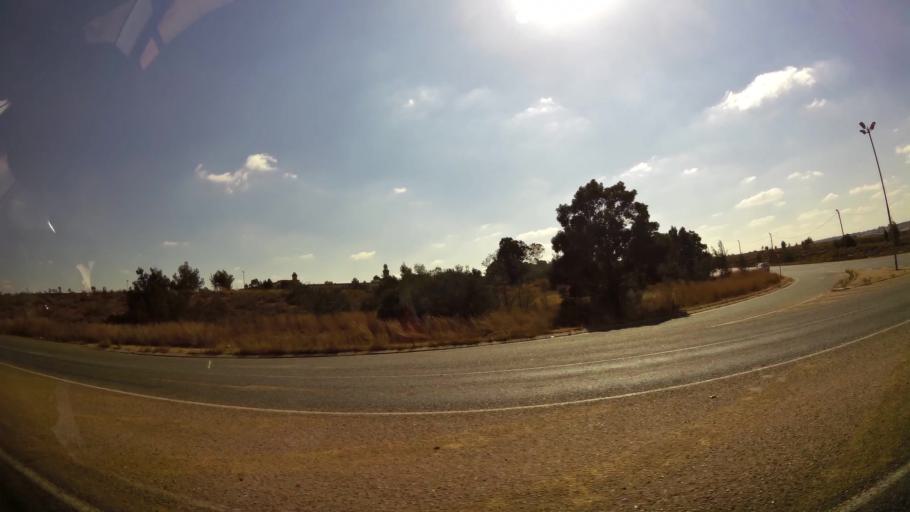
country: ZA
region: Gauteng
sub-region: West Rand District Municipality
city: Randfontein
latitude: -26.1796
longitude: 27.7596
